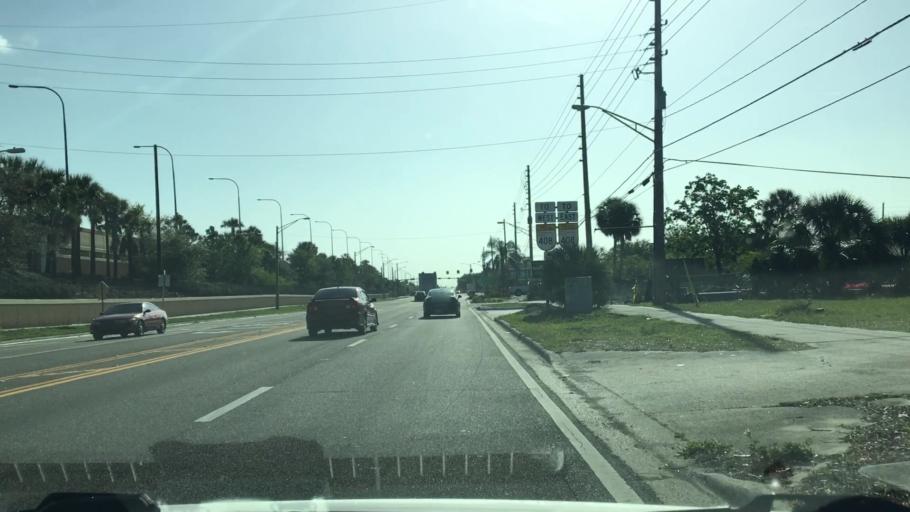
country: US
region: Florida
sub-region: Orange County
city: Azalea Park
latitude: 28.5389
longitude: -81.3140
